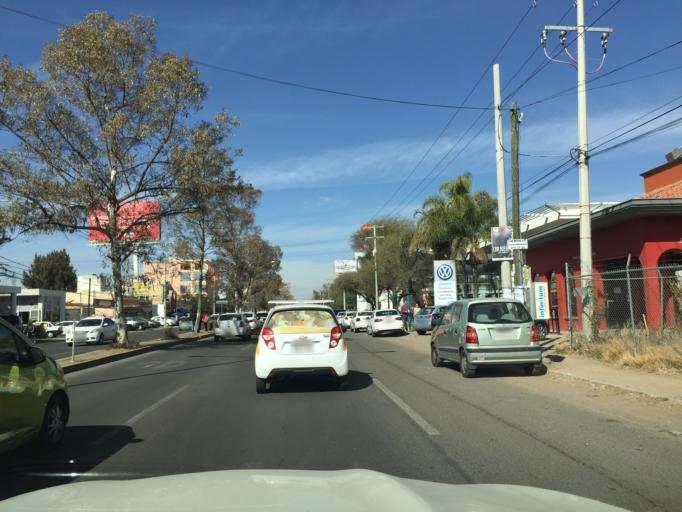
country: MX
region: Aguascalientes
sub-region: Jesus Maria
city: El Llano
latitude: 21.9204
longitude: -102.2977
